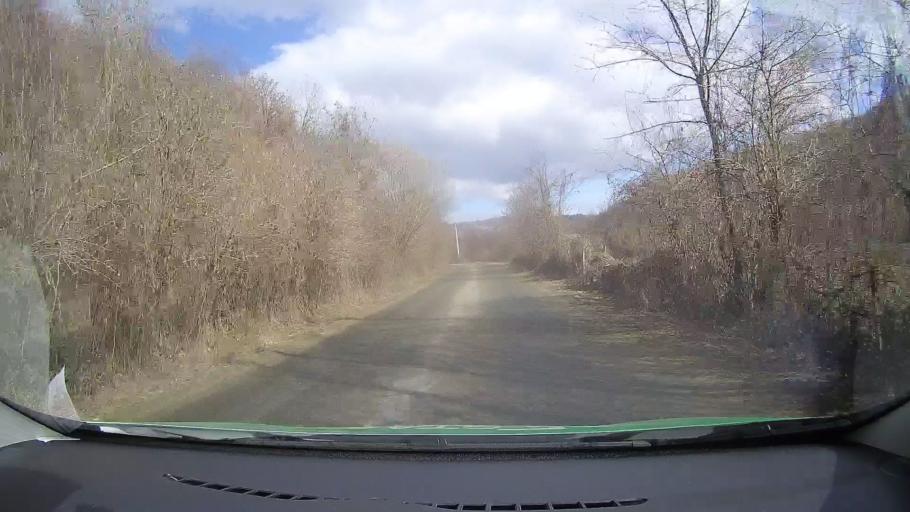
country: RO
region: Dambovita
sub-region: Comuna Motaeni
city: Motaeni
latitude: 45.1057
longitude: 25.4421
